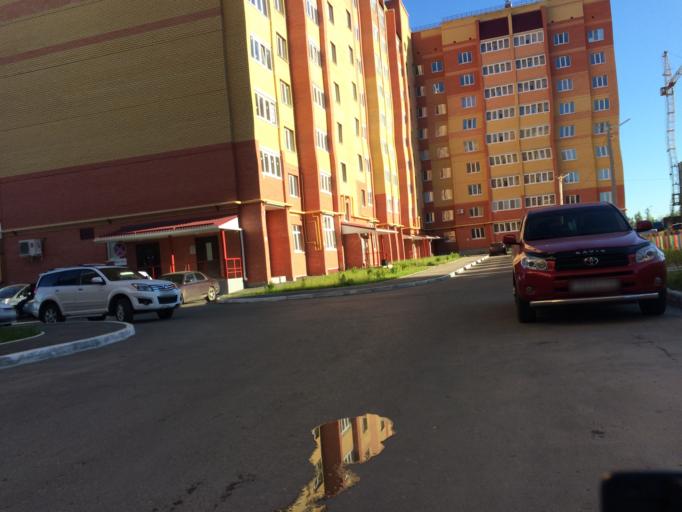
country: RU
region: Mariy-El
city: Medvedevo
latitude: 56.6465
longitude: 47.8320
